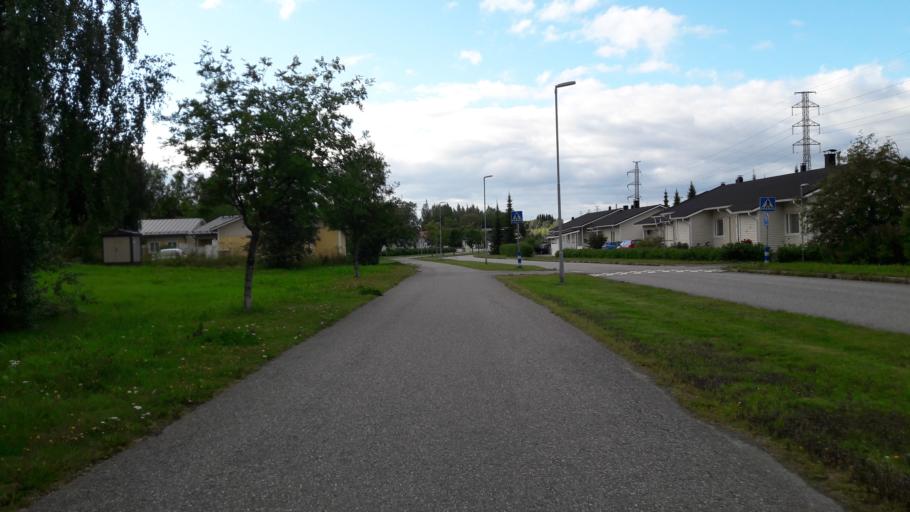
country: FI
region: North Karelia
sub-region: Joensuu
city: Joensuu
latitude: 62.5959
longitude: 29.7958
